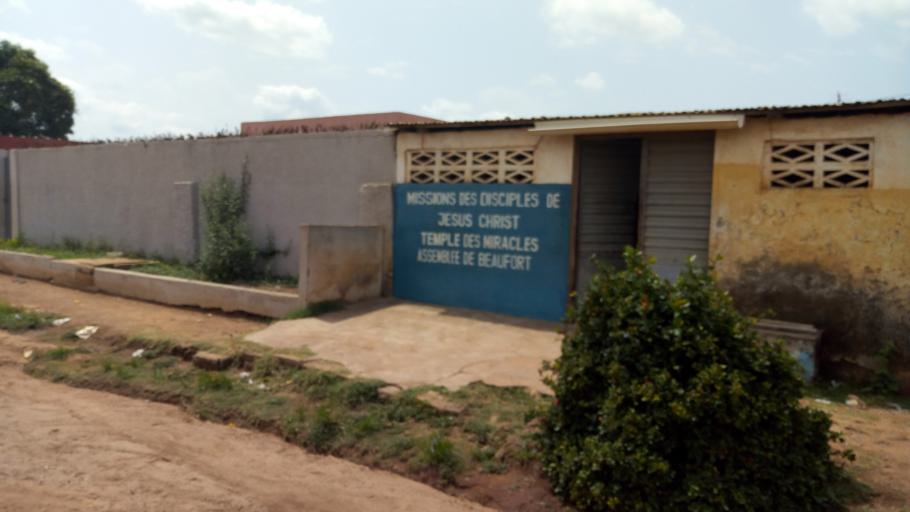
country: CI
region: Vallee du Bandama
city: Bouake
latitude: 7.7178
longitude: -5.0431
